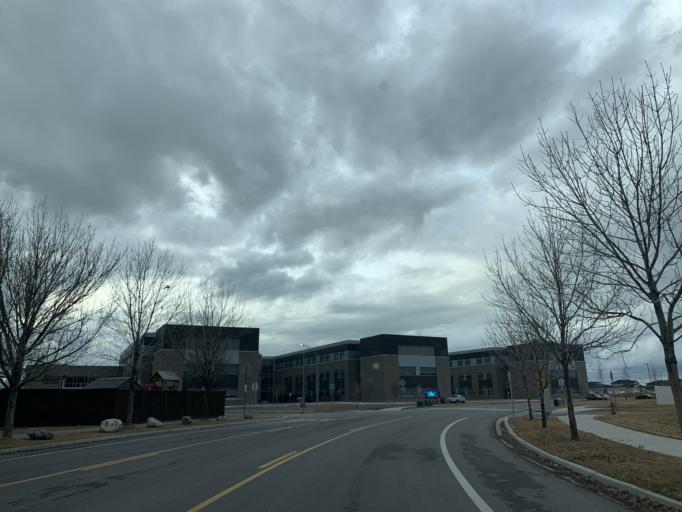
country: US
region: Utah
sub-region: Utah County
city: Orem
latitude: 40.2490
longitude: -111.7131
